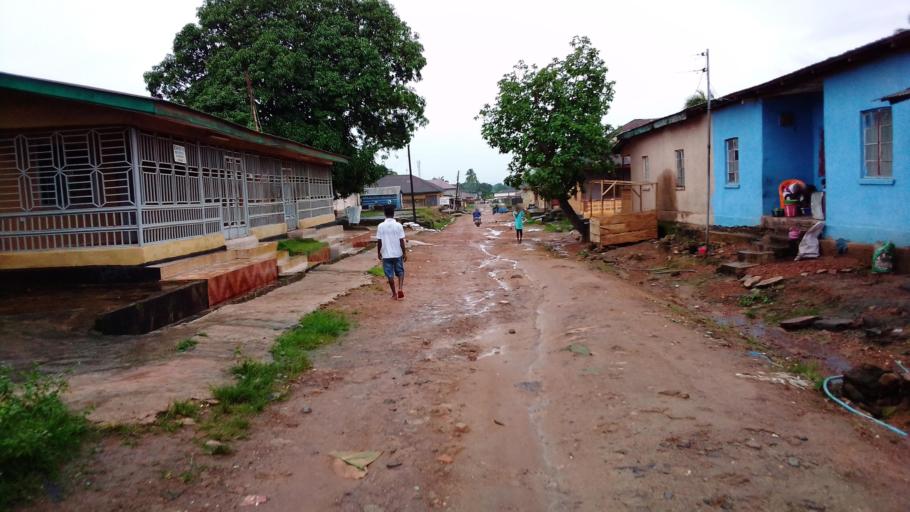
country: SL
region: Eastern Province
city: Kenema
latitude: 7.8893
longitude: -11.1900
